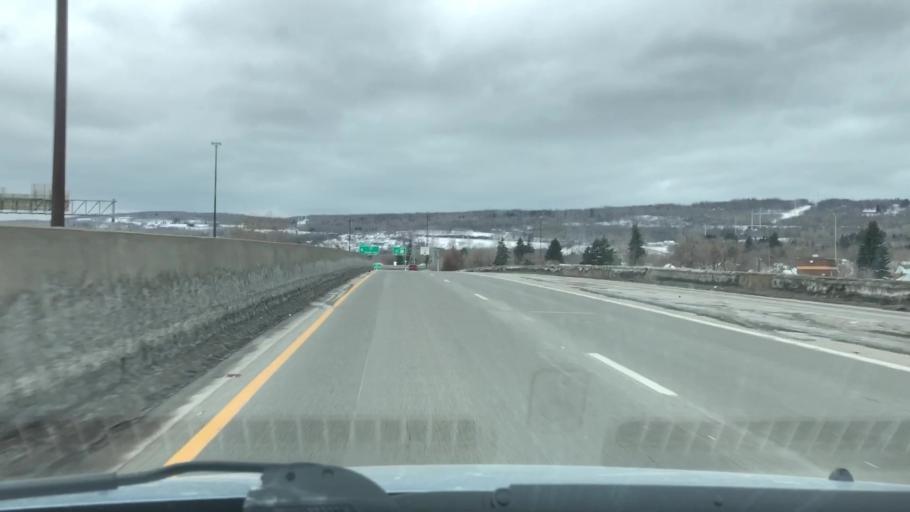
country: US
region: Minnesota
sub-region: Saint Louis County
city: Proctor
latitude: 46.7363
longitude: -92.1699
